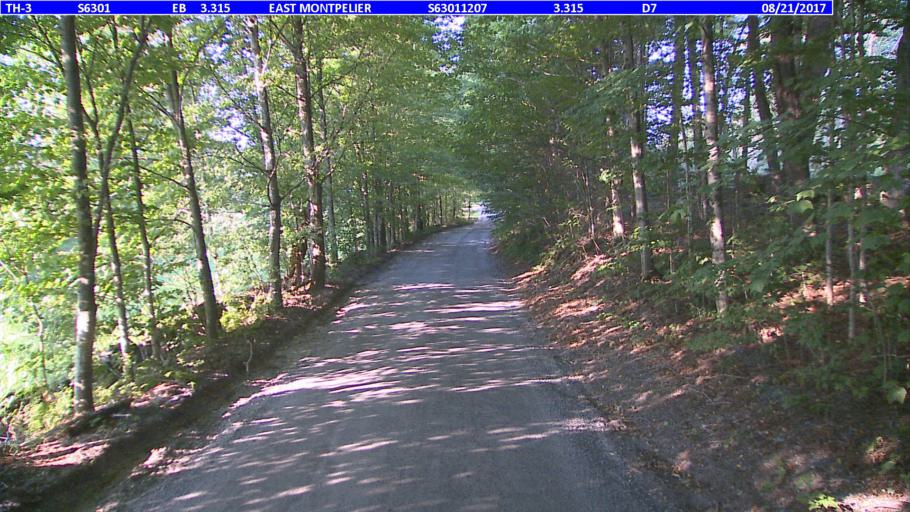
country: US
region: Vermont
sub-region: Washington County
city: Montpelier
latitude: 44.3046
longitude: -72.5121
